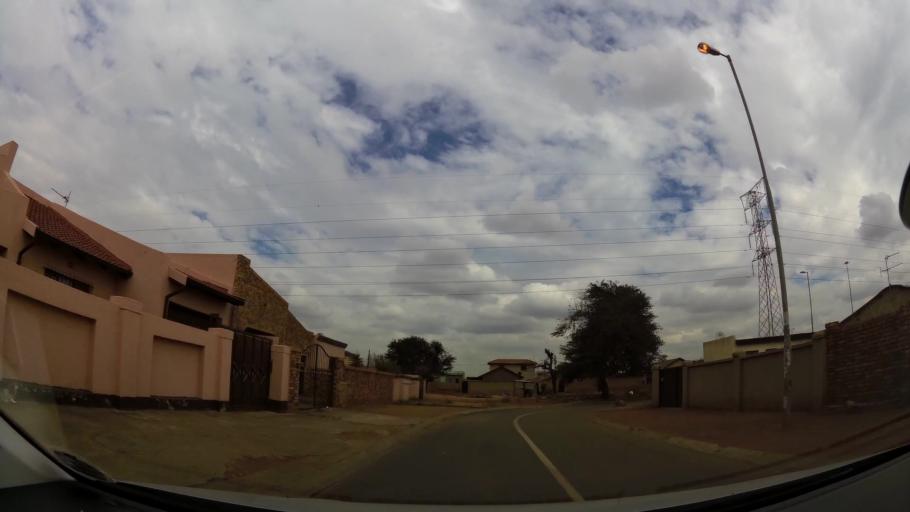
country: ZA
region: Gauteng
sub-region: City of Johannesburg Metropolitan Municipality
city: Soweto
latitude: -26.2839
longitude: 27.8497
